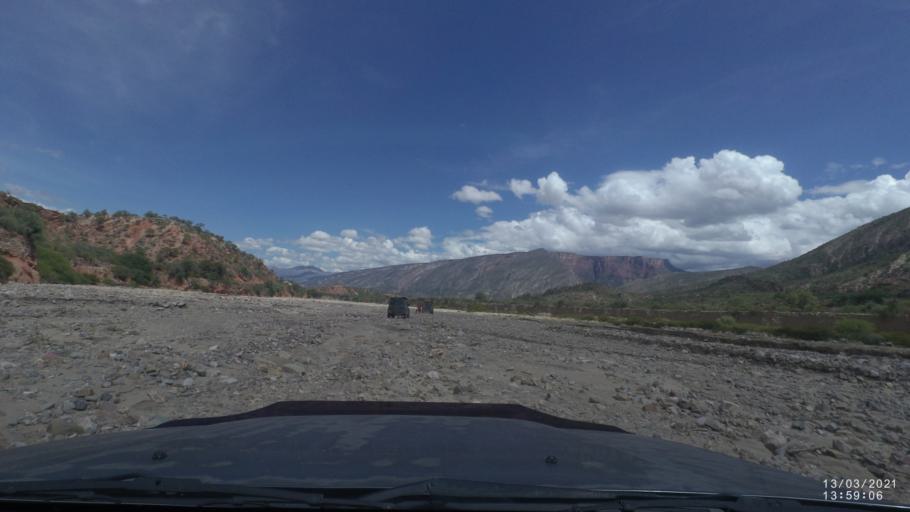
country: BO
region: Cochabamba
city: Cliza
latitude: -17.9361
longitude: -65.8645
